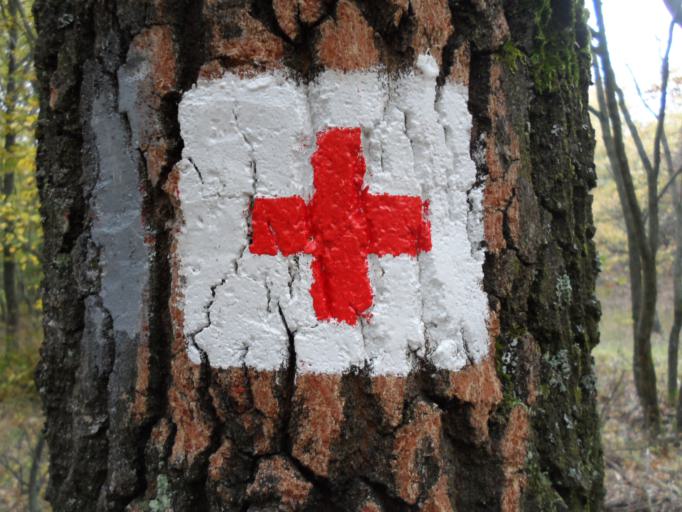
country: HU
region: Veszprem
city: Zirc
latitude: 47.3315
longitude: 17.8950
